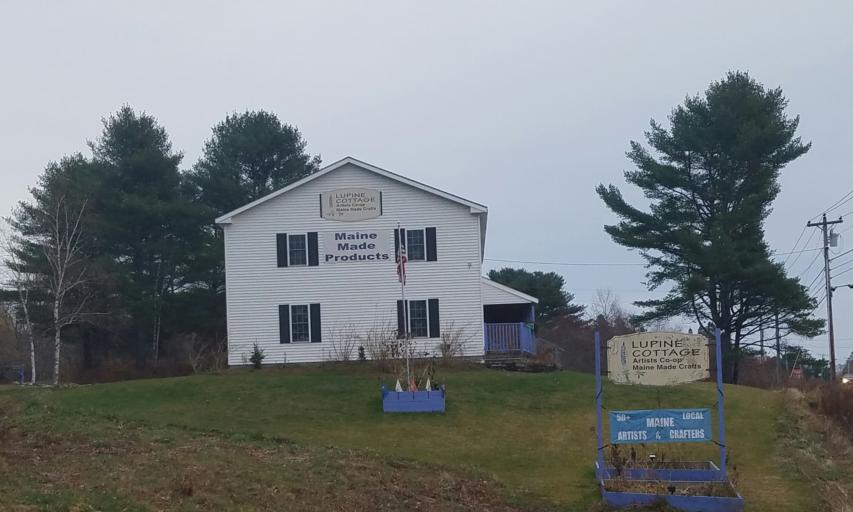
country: US
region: Maine
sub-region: Waldo County
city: Belfast
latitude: 44.4331
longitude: -68.9962
